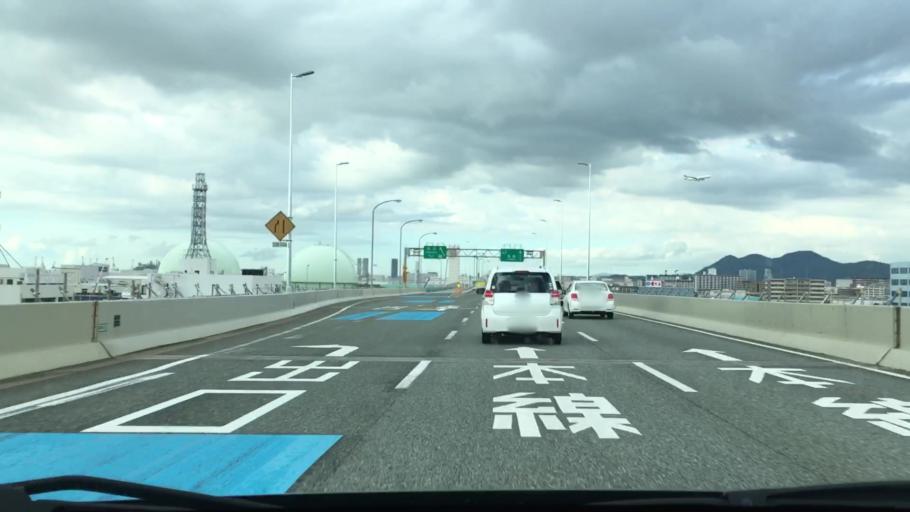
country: JP
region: Fukuoka
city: Fukuoka-shi
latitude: 33.6136
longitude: 130.4103
